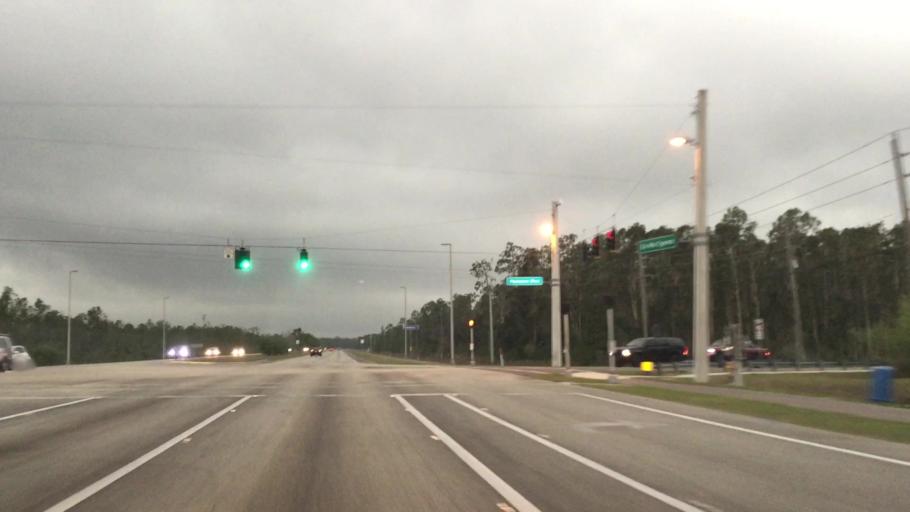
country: US
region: Florida
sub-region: Lee County
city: Villas
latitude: 26.5709
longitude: -81.8278
